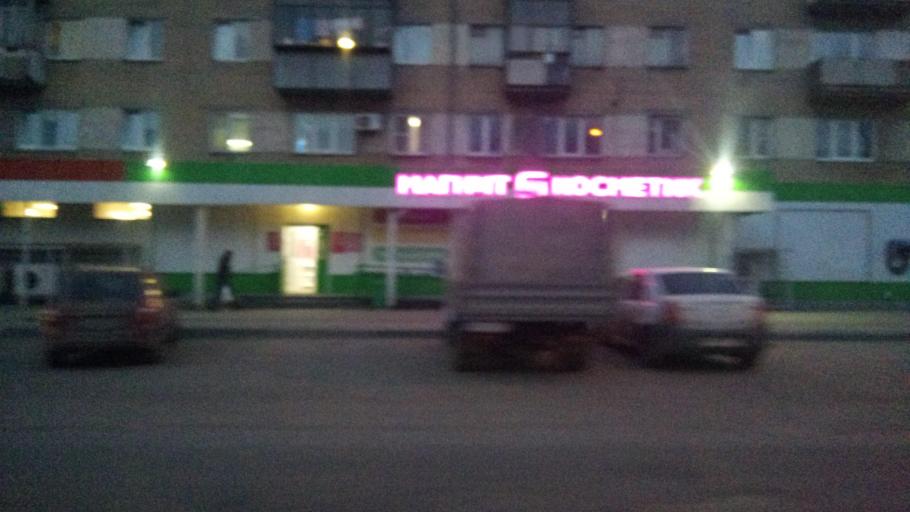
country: RU
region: Chelyabinsk
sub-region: Gorod Chelyabinsk
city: Chelyabinsk
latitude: 55.1689
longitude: 61.4614
